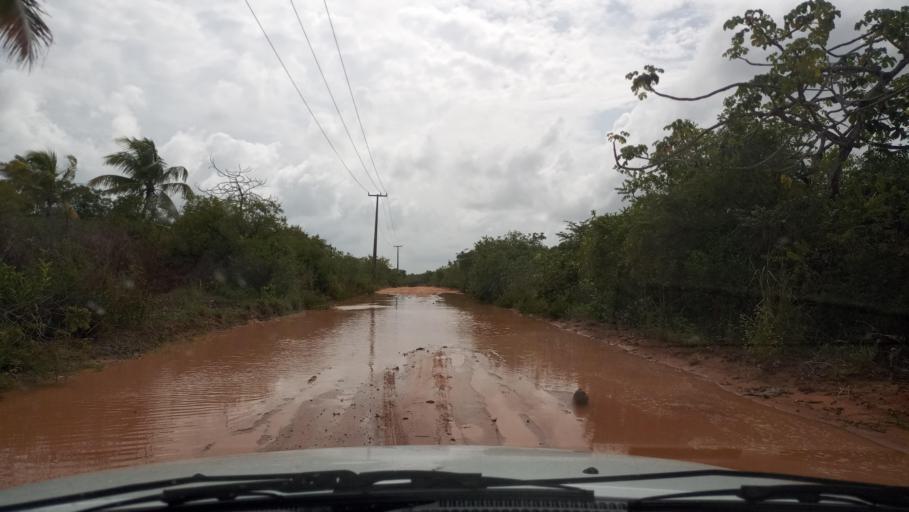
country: BR
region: Rio Grande do Norte
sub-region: Maxaranguape
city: Sao Miguel
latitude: -5.4832
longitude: -35.3230
